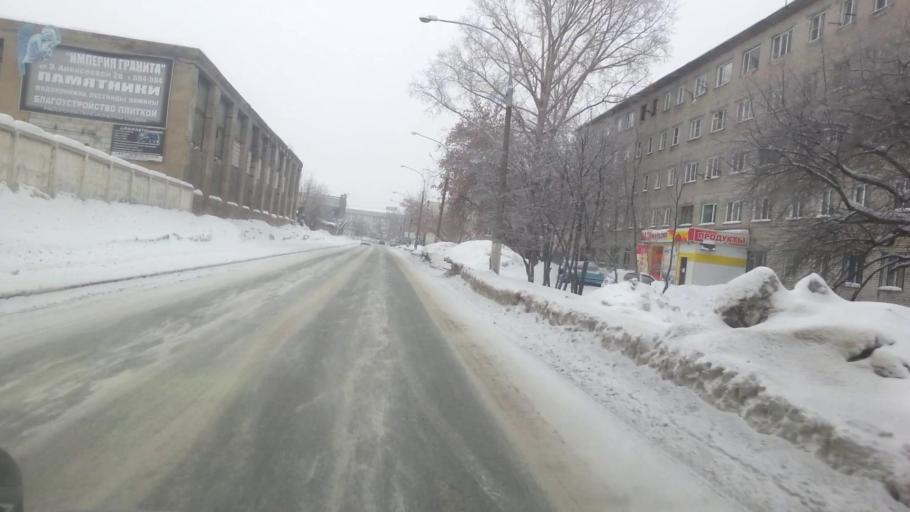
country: RU
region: Altai Krai
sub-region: Gorod Barnaulskiy
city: Barnaul
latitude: 53.3816
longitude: 83.7353
